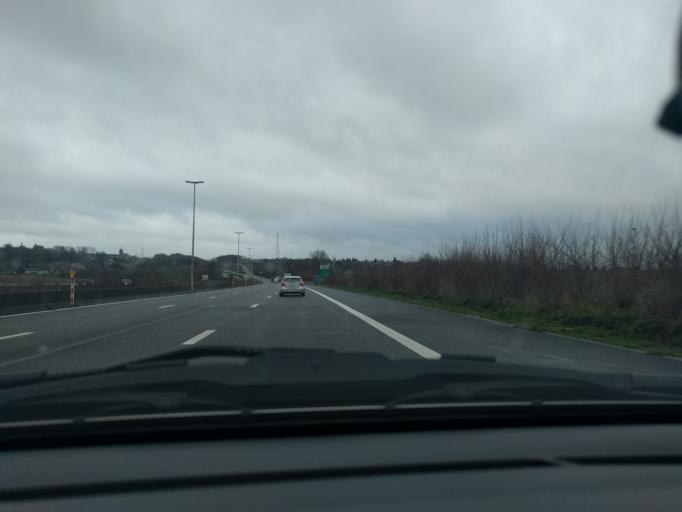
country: BE
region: Wallonia
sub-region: Province de Namur
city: Namur
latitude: 50.5043
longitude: 4.8860
